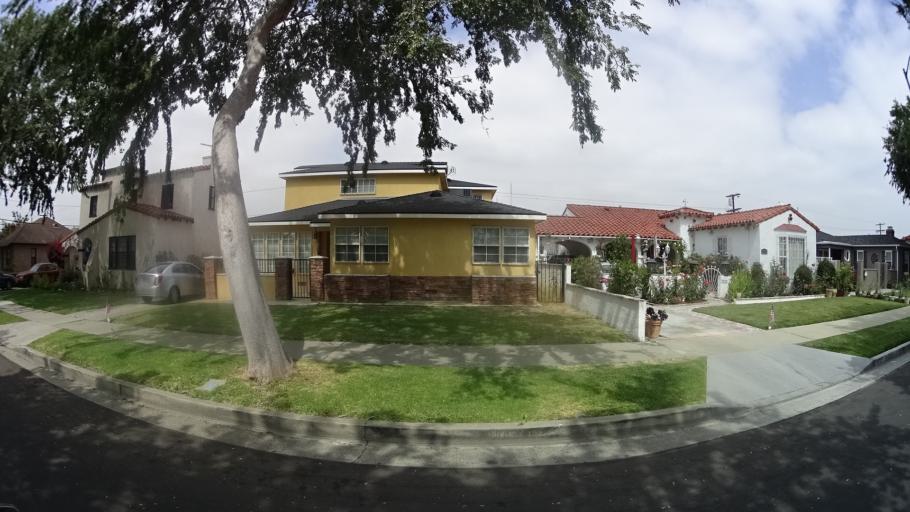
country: US
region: California
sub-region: Los Angeles County
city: View Park-Windsor Hills
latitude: 34.0188
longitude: -118.3393
